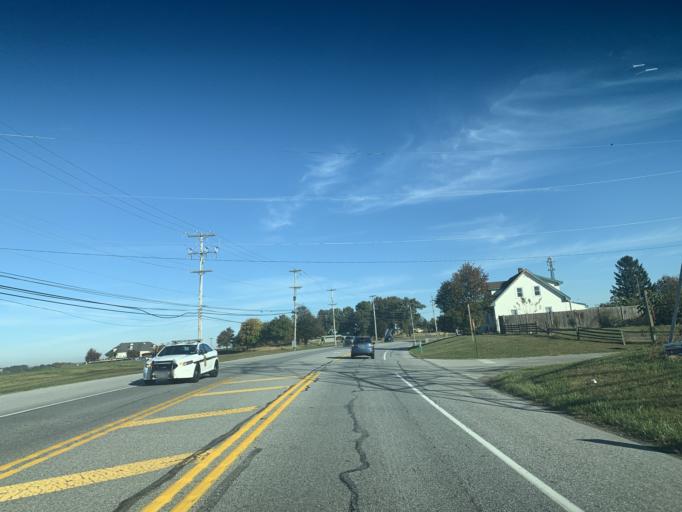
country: US
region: Pennsylvania
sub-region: Chester County
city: Oxford
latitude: 39.8114
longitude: -75.9683
